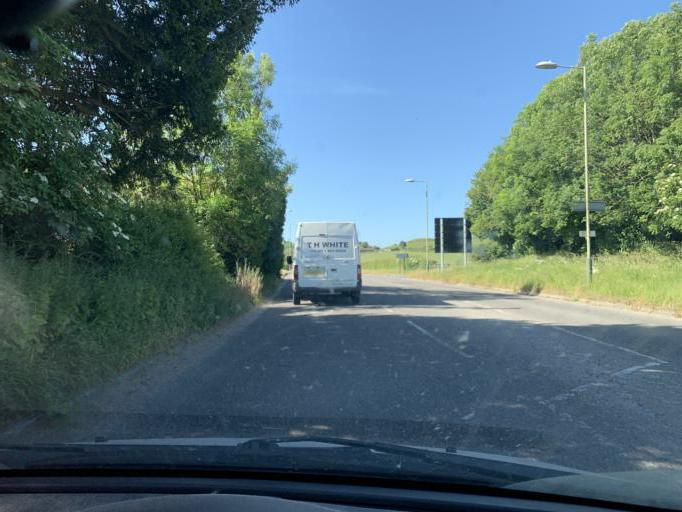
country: GB
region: England
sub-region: Wiltshire
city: Salisbury
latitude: 51.0984
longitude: -1.7968
